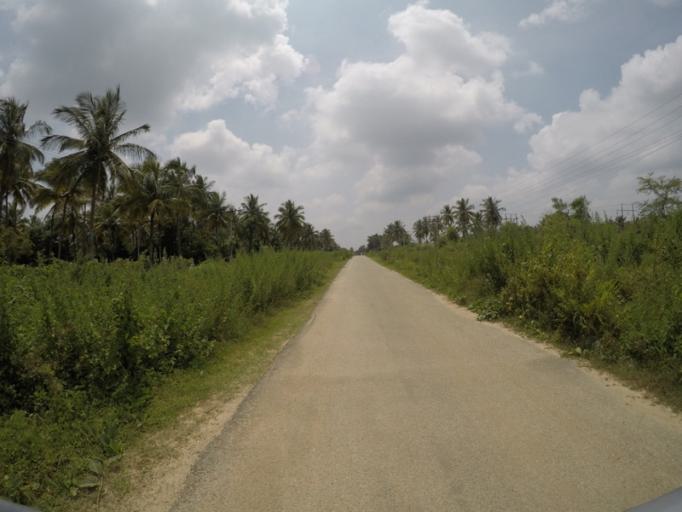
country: IN
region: Karnataka
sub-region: Ramanagara
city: Kanakapura
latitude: 12.7093
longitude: 77.4747
